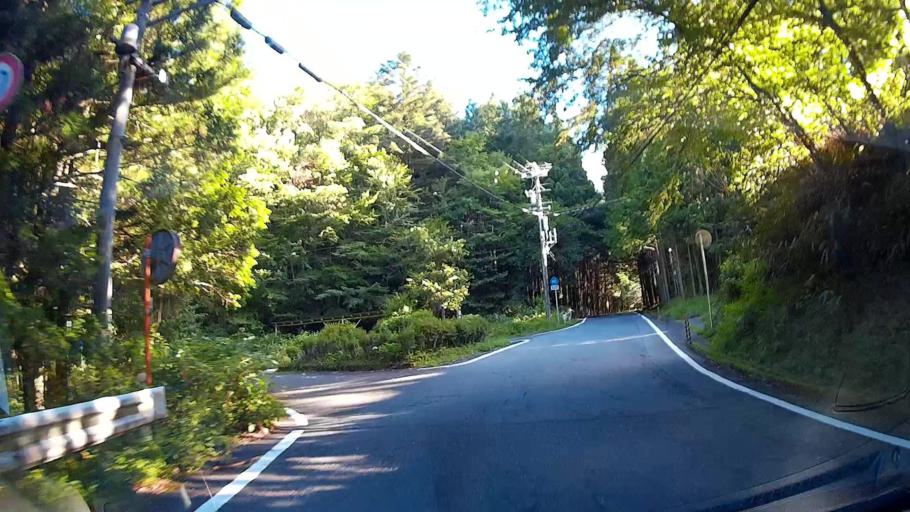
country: JP
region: Shizuoka
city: Shizuoka-shi
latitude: 35.2198
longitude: 138.2303
